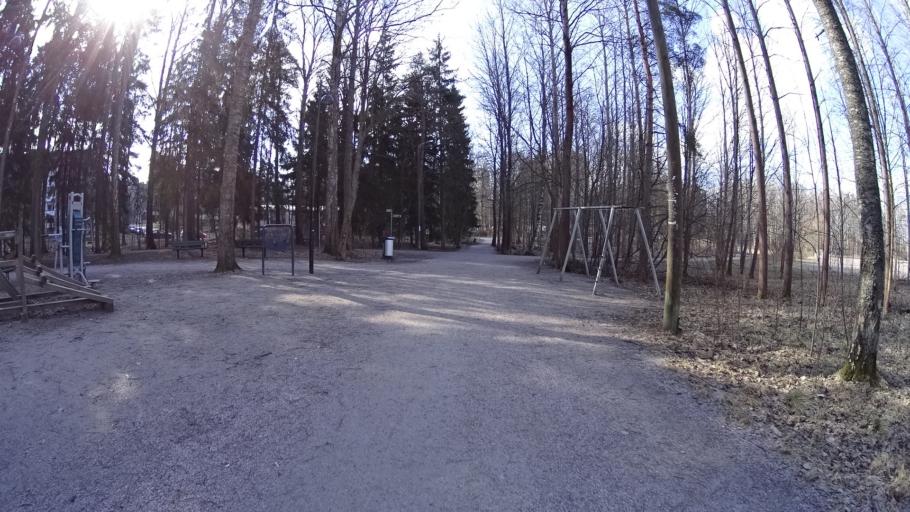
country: FI
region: Uusimaa
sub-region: Helsinki
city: Teekkarikylae
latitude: 60.2103
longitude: 24.8683
